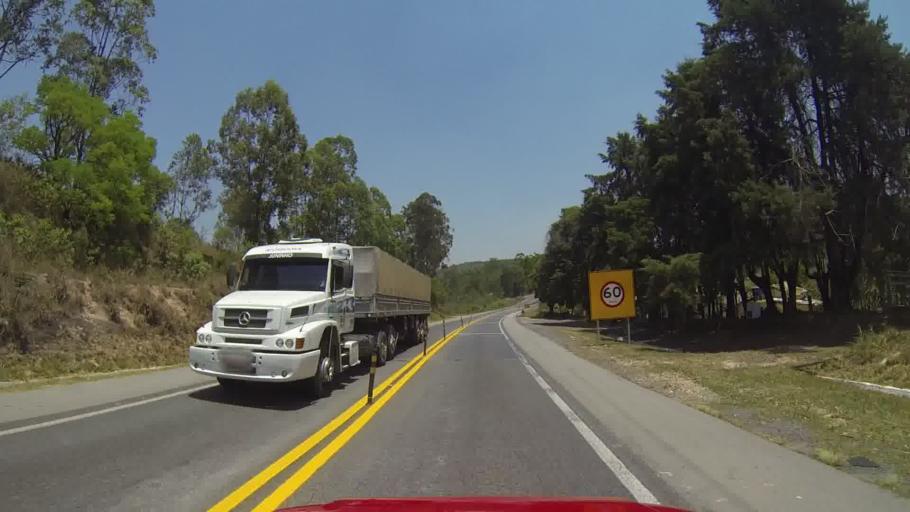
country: BR
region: Minas Gerais
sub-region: Itapecerica
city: Itapecerica
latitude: -20.2962
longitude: -45.1787
